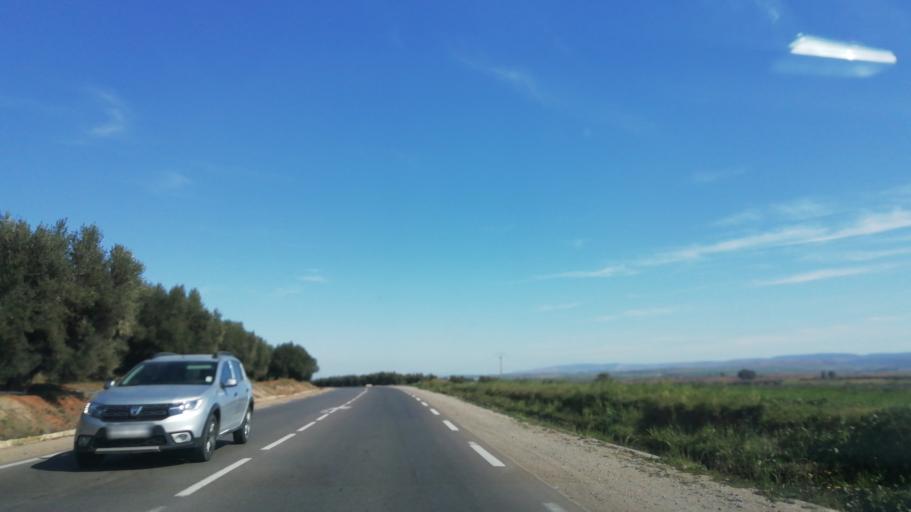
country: DZ
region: Mascara
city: Oued el Abtal
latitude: 35.4195
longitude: 0.4283
